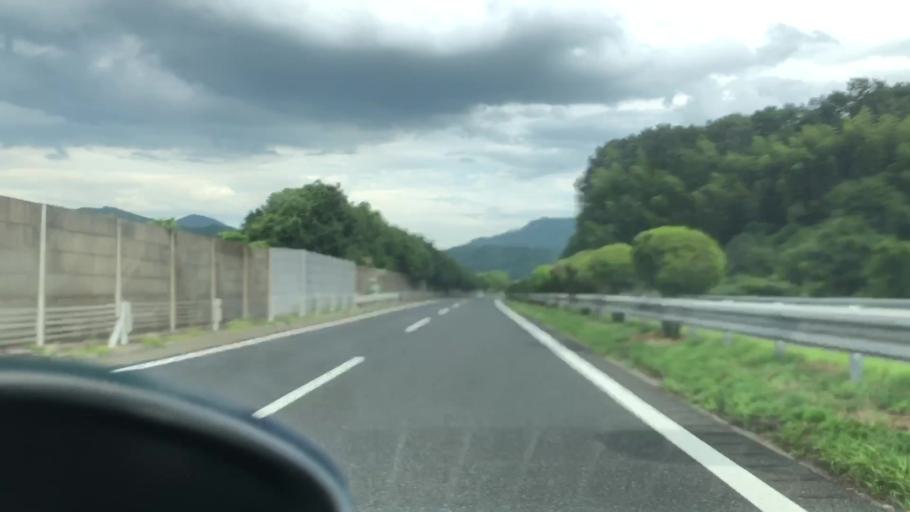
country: JP
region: Hyogo
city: Yamazakicho-nakabirose
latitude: 34.9690
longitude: 134.6720
